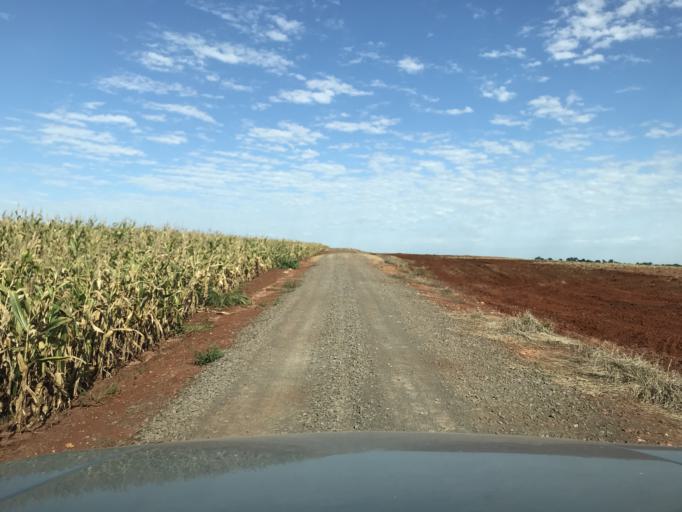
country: BR
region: Parana
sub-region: Palotina
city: Palotina
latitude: -24.1587
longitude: -53.7435
